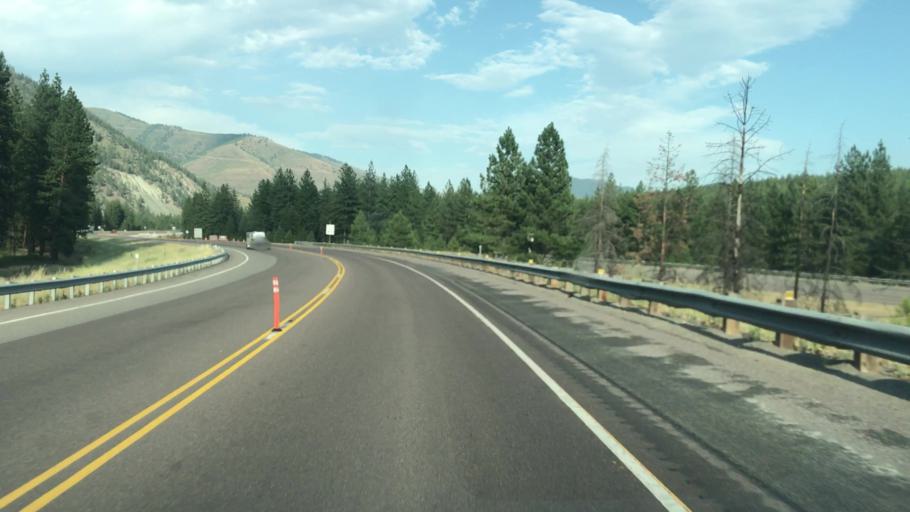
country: US
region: Montana
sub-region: Mineral County
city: Superior
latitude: 47.0175
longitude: -114.6692
